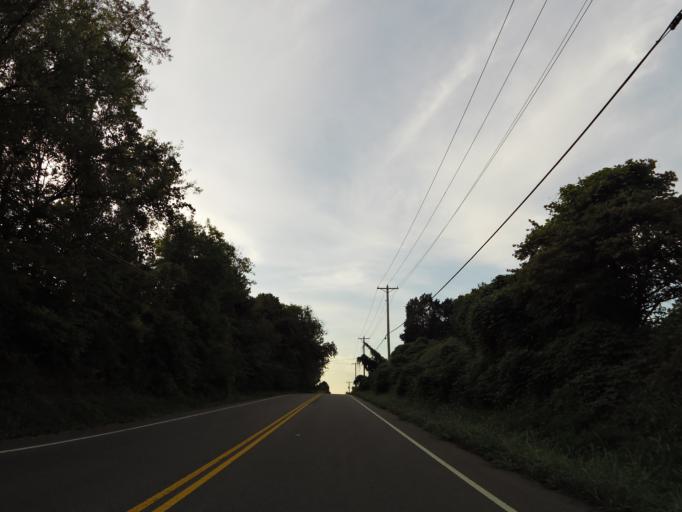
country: US
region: Tennessee
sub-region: Blount County
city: Eagleton Village
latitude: 35.8511
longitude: -83.9425
